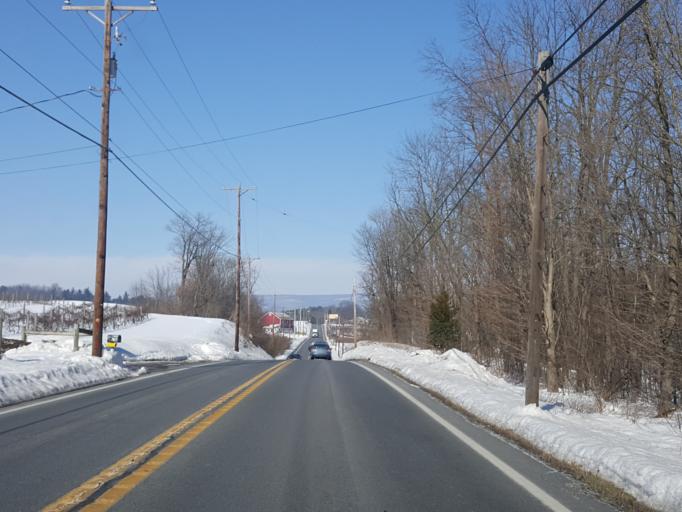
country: US
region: Pennsylvania
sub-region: Berks County
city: Womelsdorf
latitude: 40.4616
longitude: -76.1434
